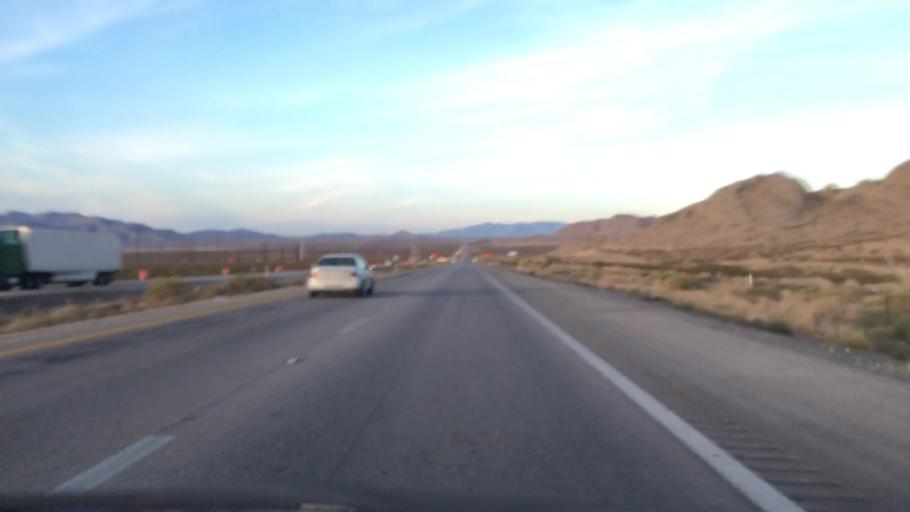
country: US
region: Nevada
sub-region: Clark County
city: Nellis Air Force Base
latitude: 36.3883
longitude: -114.8869
